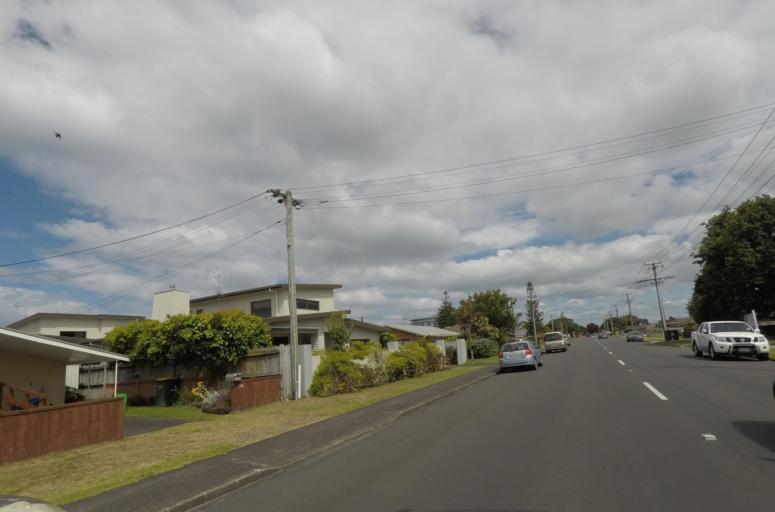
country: NZ
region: Auckland
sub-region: Auckland
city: Rothesay Bay
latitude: -36.5835
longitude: 174.6905
